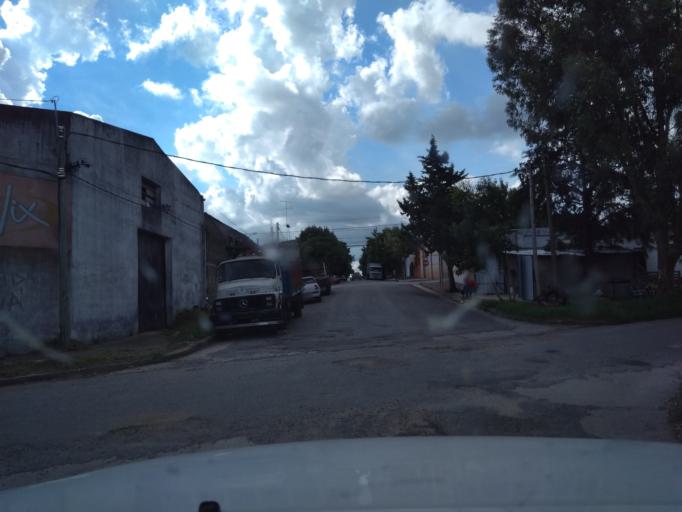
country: UY
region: Florida
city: Florida
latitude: -34.0912
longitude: -56.2152
